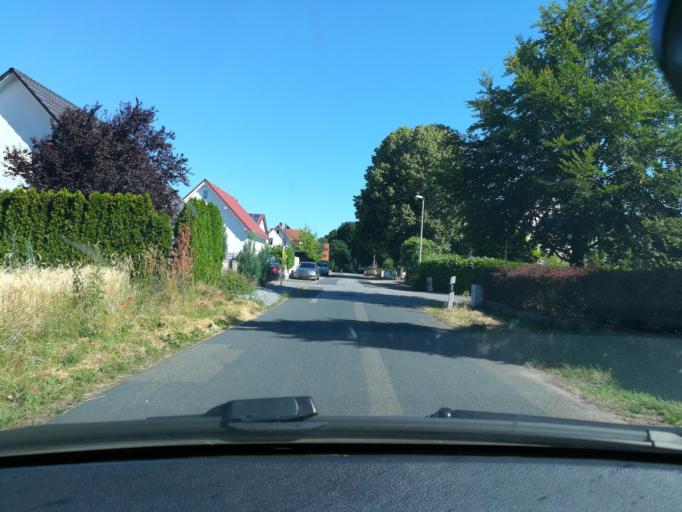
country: DE
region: North Rhine-Westphalia
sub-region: Regierungsbezirk Detmold
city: Minden
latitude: 52.3133
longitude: 8.9282
